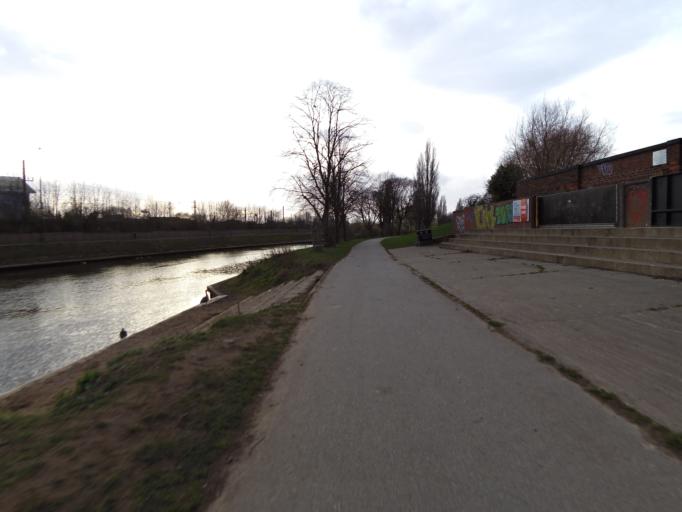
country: GB
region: England
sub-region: City of York
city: York
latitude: 53.9618
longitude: -1.0945
